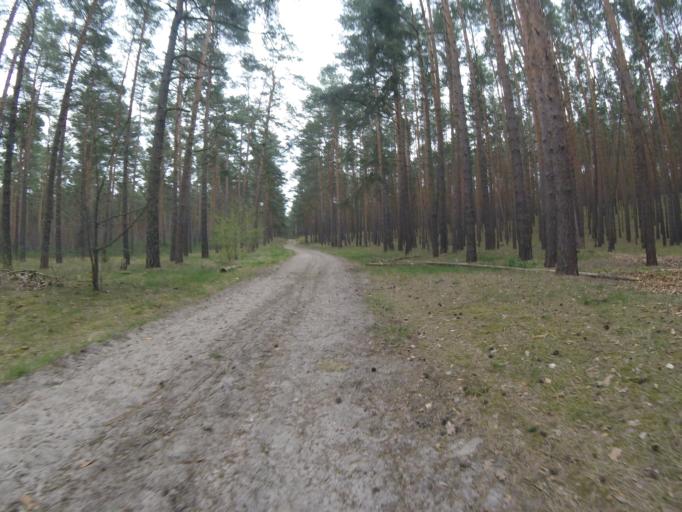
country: DE
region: Brandenburg
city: Schwerin
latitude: 52.1434
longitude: 13.6397
